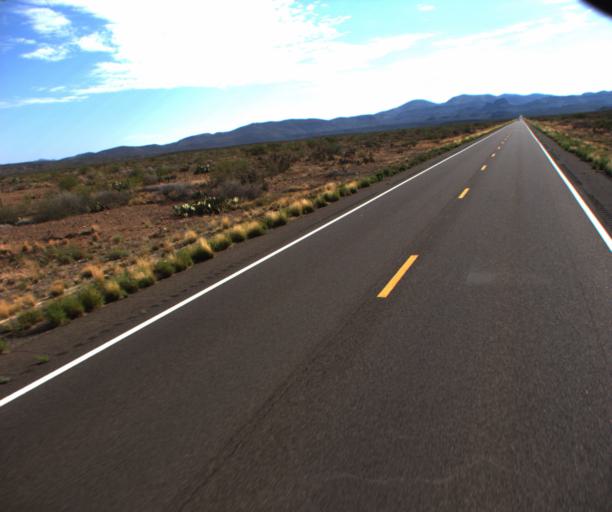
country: US
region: Arizona
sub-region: Graham County
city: Safford
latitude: 32.8218
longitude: -109.4734
